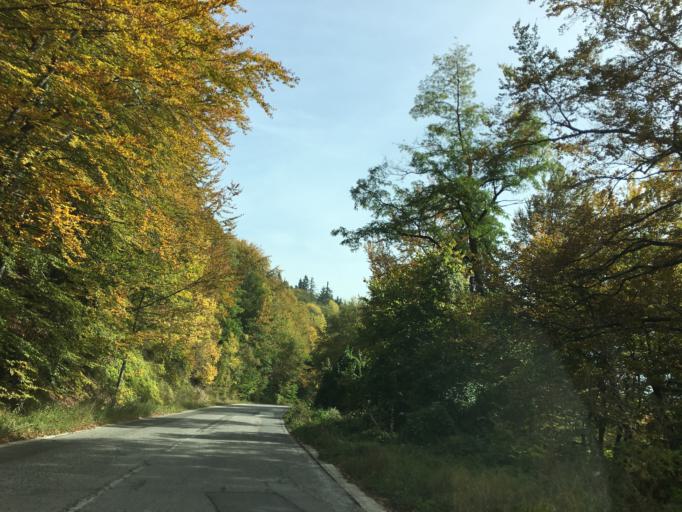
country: BG
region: Sofiya
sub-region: Obshtina Samokov
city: Samokov
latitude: 42.2854
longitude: 23.6458
